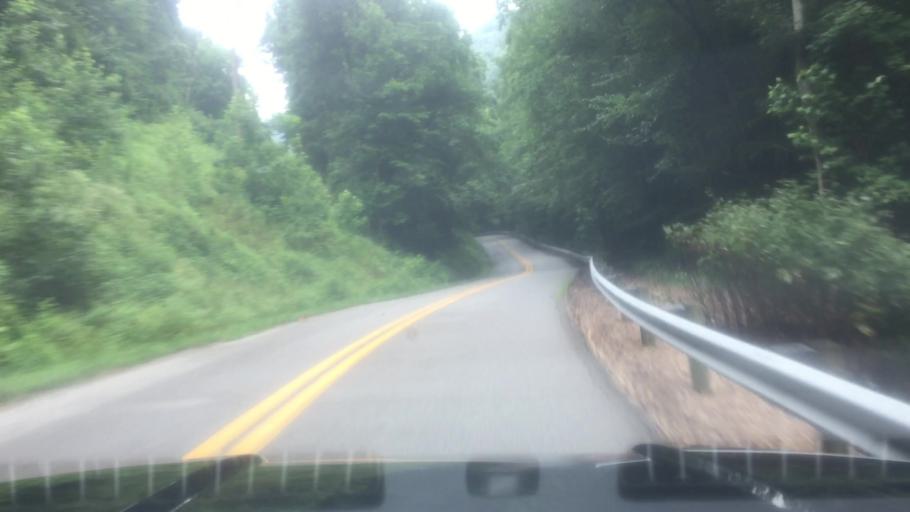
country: US
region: West Virginia
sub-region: Kanawha County
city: Montgomery
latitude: 38.1074
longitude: -81.3864
